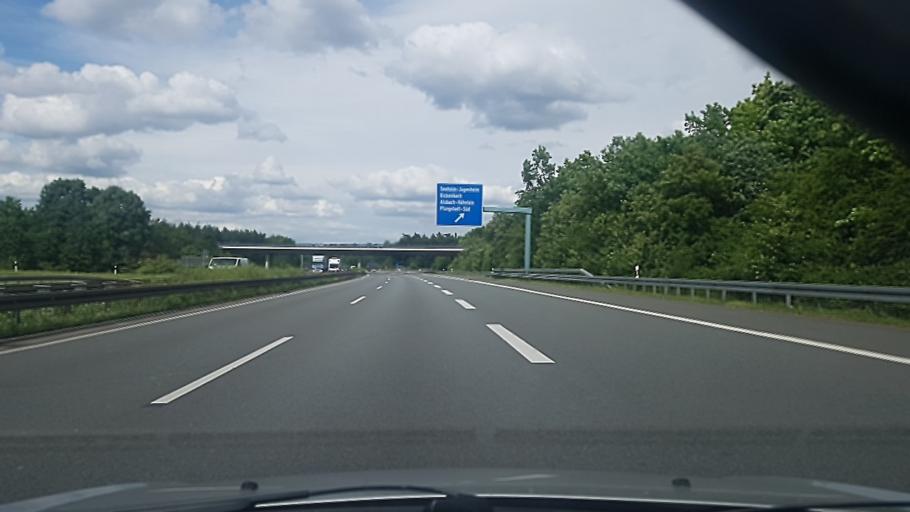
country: DE
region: Hesse
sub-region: Regierungsbezirk Darmstadt
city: Bickenbach
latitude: 49.7748
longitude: 8.6095
